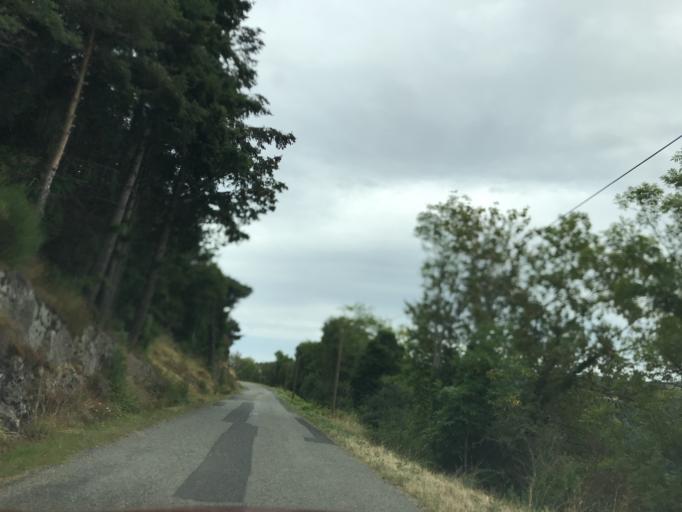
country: FR
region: Rhone-Alpes
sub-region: Departement de la Loire
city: Sail-sous-Couzan
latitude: 45.6924
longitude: 3.9199
